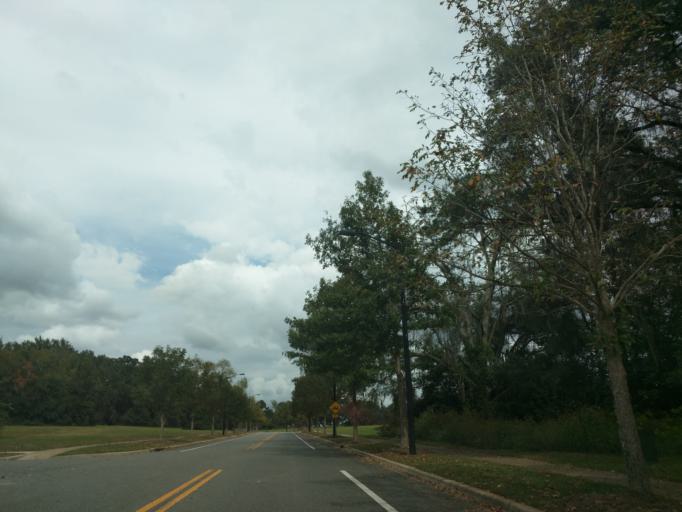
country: US
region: Florida
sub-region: Leon County
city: Woodville
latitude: 30.3875
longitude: -84.2095
